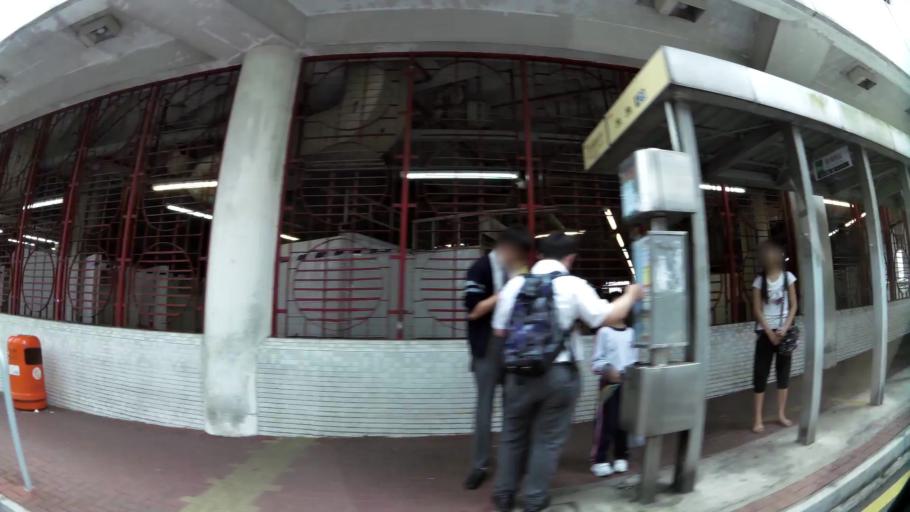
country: HK
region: Tsuen Wan
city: Tsuen Wan
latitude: 22.3786
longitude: 114.1042
